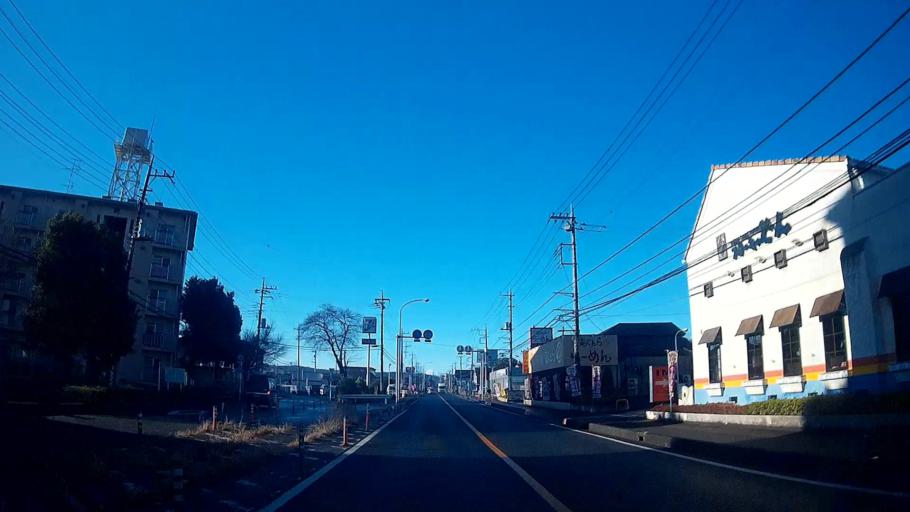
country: JP
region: Saitama
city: Sayama
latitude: 35.8540
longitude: 139.3781
